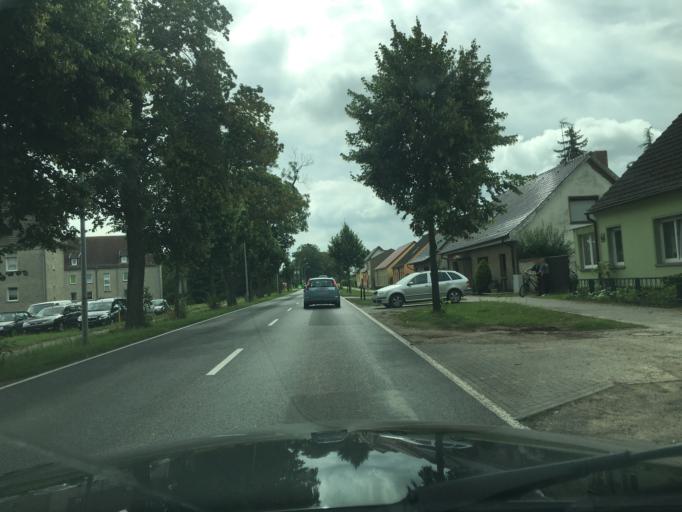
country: DE
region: Brandenburg
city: Oranienburg
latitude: 52.8499
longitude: 13.1744
